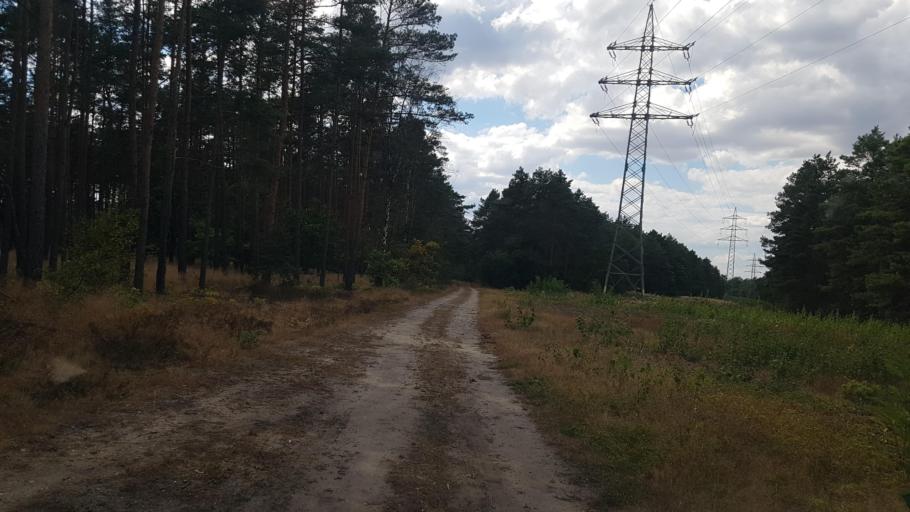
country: DE
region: Brandenburg
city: Finsterwalde
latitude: 51.6375
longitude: 13.7517
